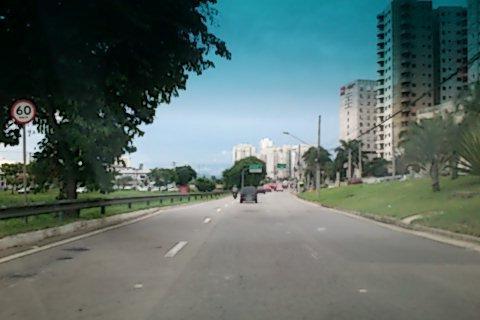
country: BR
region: Sao Paulo
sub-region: Sao Jose Dos Campos
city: Sao Jose dos Campos
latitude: -23.2072
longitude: -45.9045
